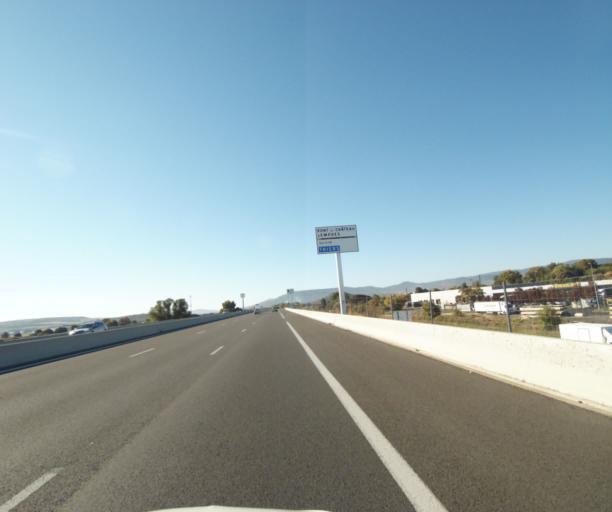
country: FR
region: Auvergne
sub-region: Departement du Puy-de-Dome
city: Aulnat
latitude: 45.7965
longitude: 3.1473
